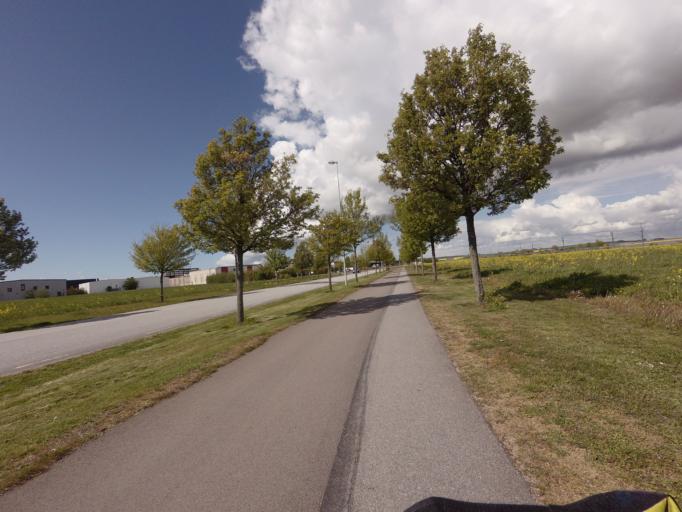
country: SE
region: Skane
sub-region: Landskrona
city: Landskrona
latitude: 55.8864
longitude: 12.8542
